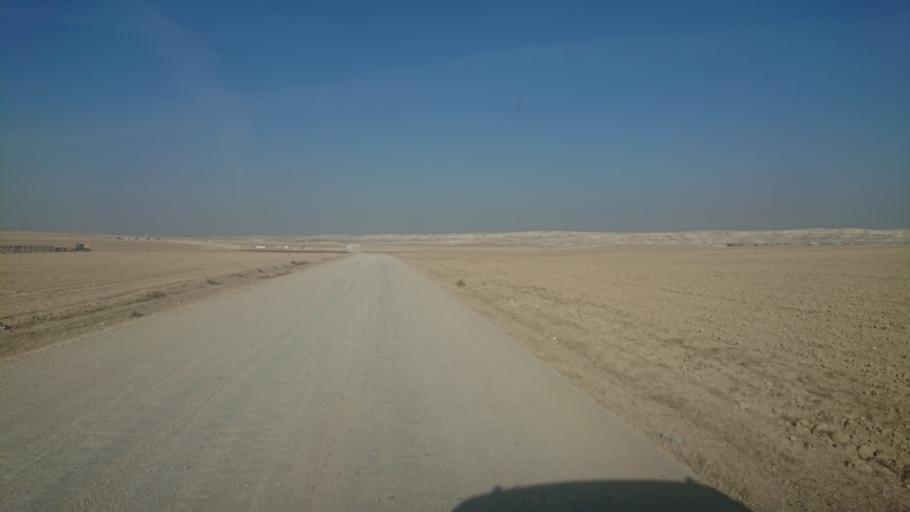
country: TR
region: Aksaray
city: Sultanhani
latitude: 38.0614
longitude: 33.6147
